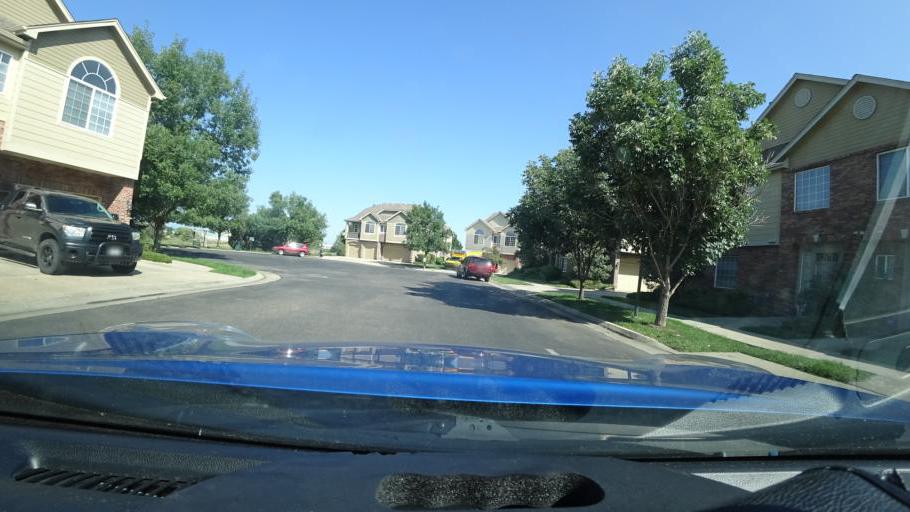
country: US
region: Colorado
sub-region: Adams County
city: Aurora
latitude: 39.7206
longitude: -104.8112
